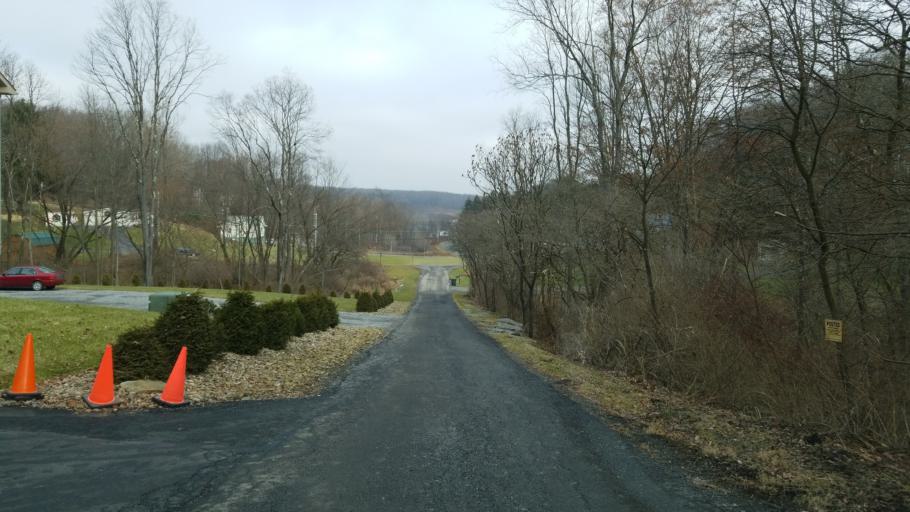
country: US
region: Pennsylvania
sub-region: Clearfield County
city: Sandy
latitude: 41.1233
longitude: -78.7812
